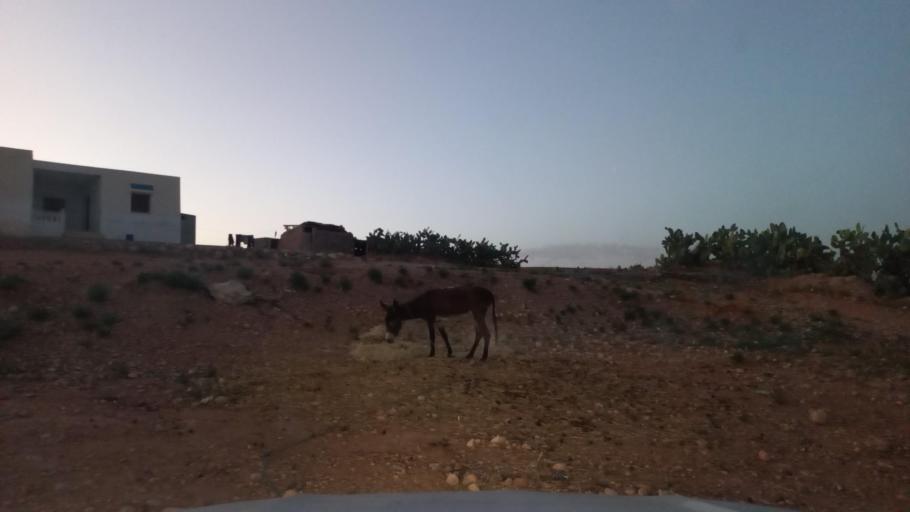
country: TN
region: Al Qasrayn
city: Sbiba
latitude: 35.3790
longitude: 9.0138
